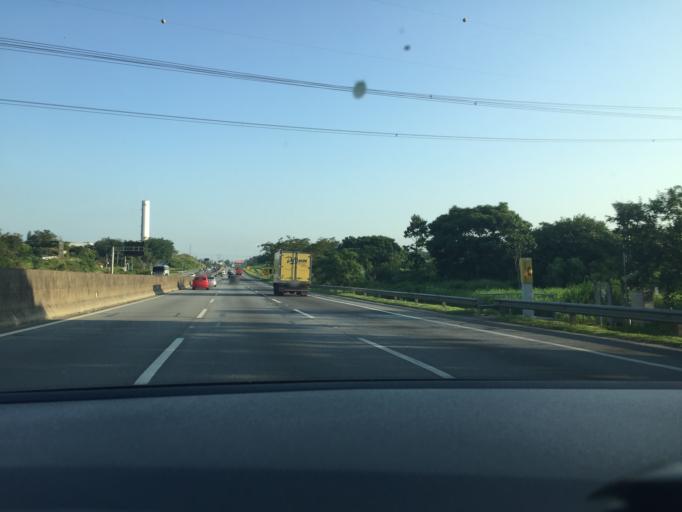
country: BR
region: Sao Paulo
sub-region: Louveira
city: Louveira
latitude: -23.1041
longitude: -46.9638
